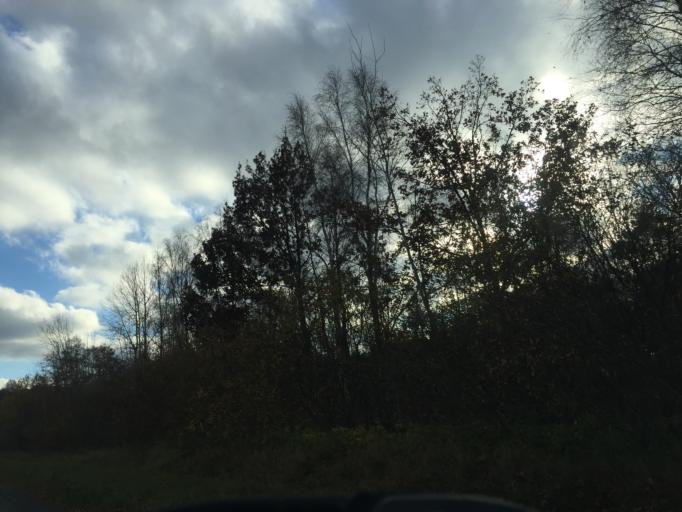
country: LV
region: Liepaja
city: Vec-Liepaja
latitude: 56.5794
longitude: 21.0401
